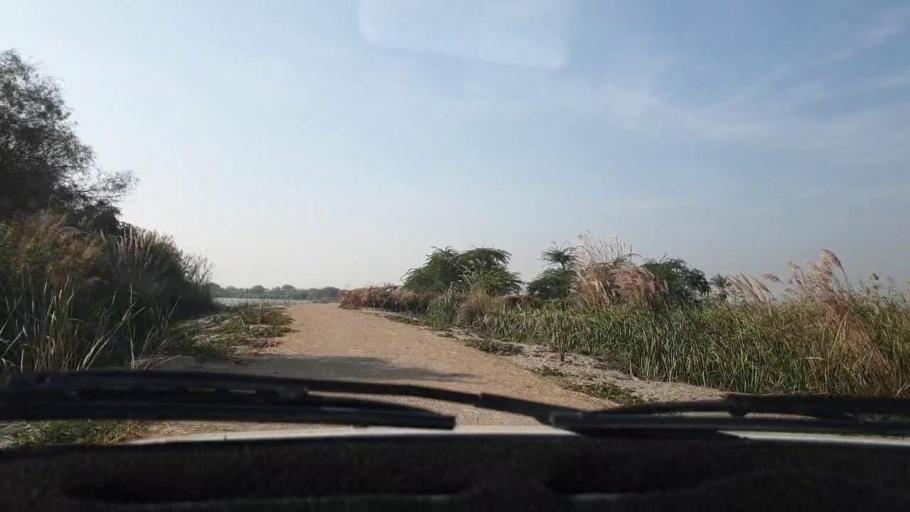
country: PK
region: Sindh
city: Tando Muhammad Khan
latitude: 24.9997
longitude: 68.4631
